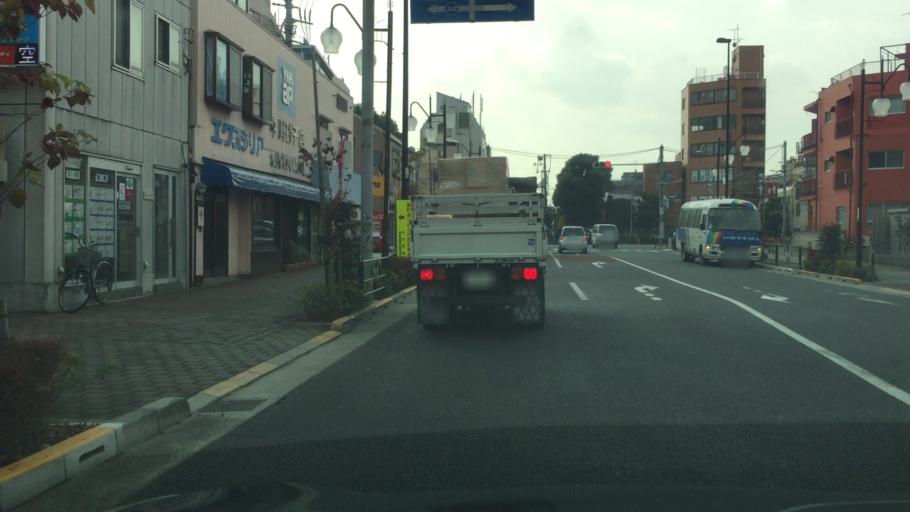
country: JP
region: Tokyo
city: Tokyo
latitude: 35.7403
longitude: 139.6878
